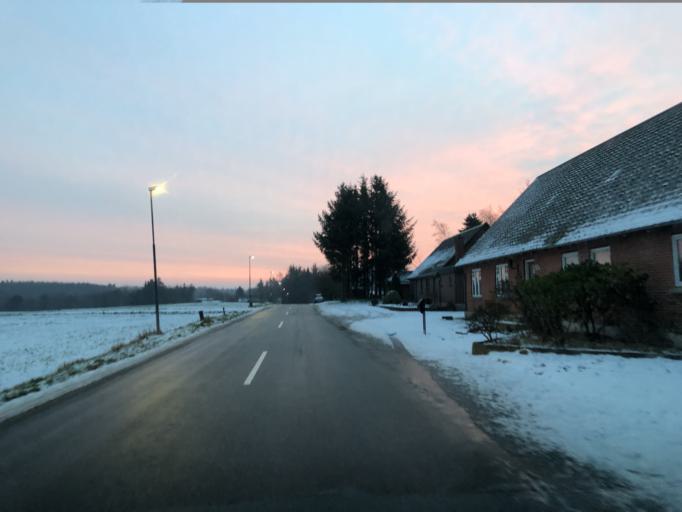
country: DK
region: Central Jutland
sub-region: Holstebro Kommune
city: Ulfborg
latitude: 56.2012
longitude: 8.4271
